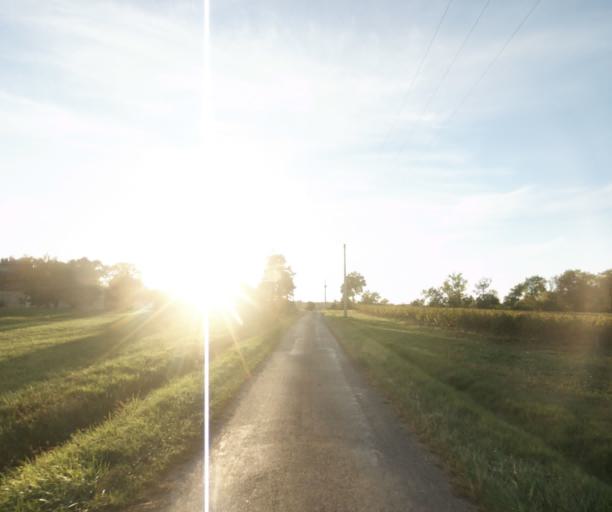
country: FR
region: Midi-Pyrenees
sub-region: Departement du Gers
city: Gondrin
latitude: 43.8611
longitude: 0.2719
